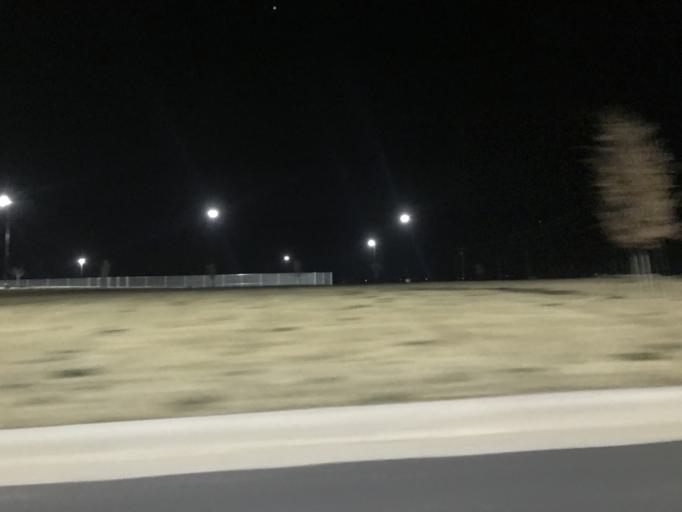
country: US
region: Texas
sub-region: Taylor County
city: Potosi
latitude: 32.3727
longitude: -99.7165
